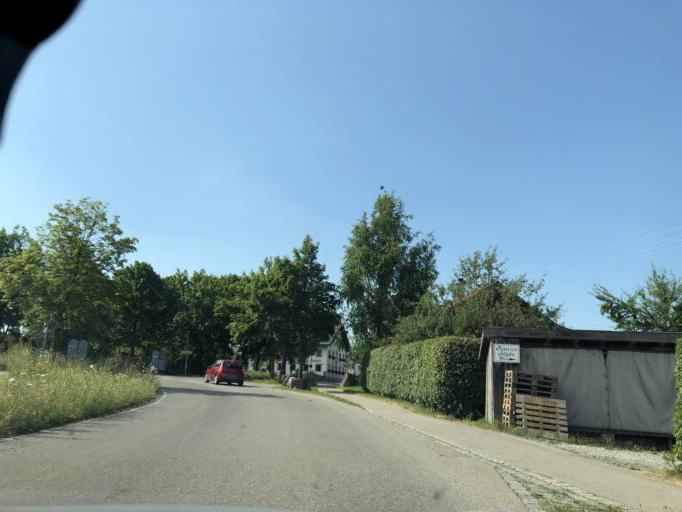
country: DE
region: Bavaria
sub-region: Swabia
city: Oy-Mittelberg
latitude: 47.6430
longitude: 10.4552
